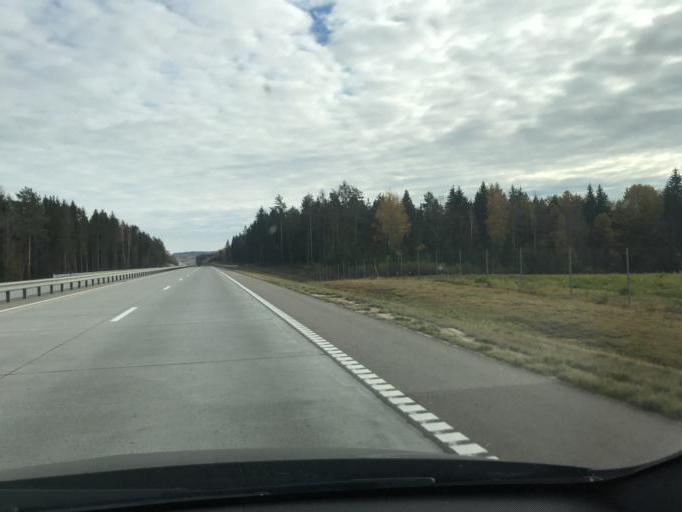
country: BY
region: Minsk
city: Zaslawye
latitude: 54.0650
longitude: 27.3179
